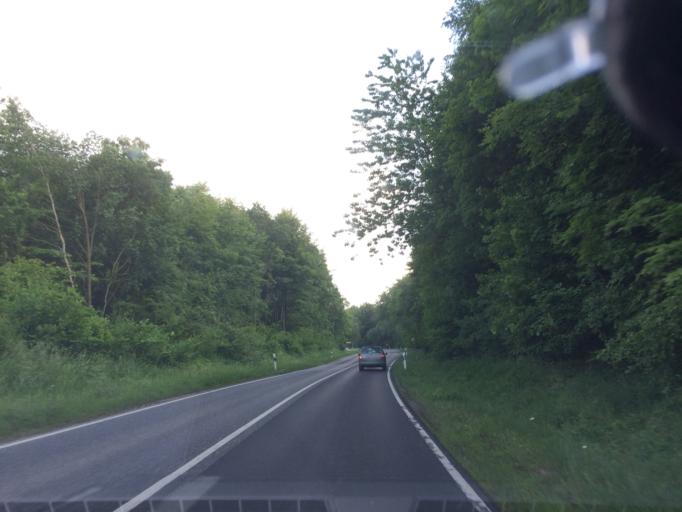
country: DE
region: Hesse
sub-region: Regierungsbezirk Kassel
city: Espenau
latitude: 51.3863
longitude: 9.4364
